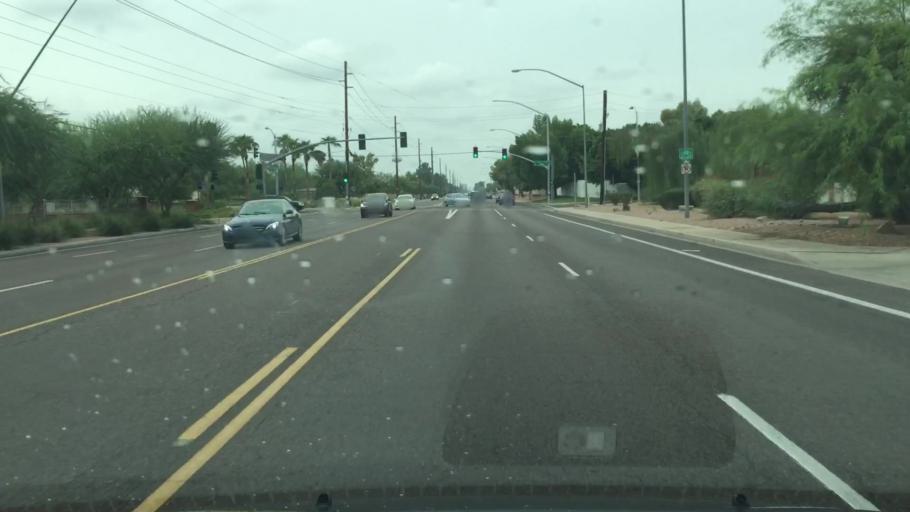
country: US
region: Arizona
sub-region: Maricopa County
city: Gilbert
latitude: 33.3936
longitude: -111.7789
